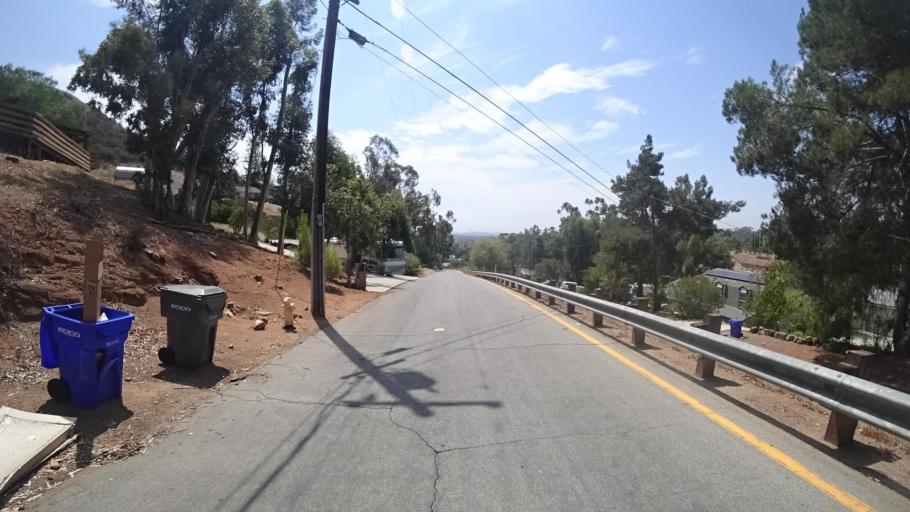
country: US
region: California
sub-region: San Diego County
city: Hidden Meadows
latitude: 33.1830
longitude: -117.0880
